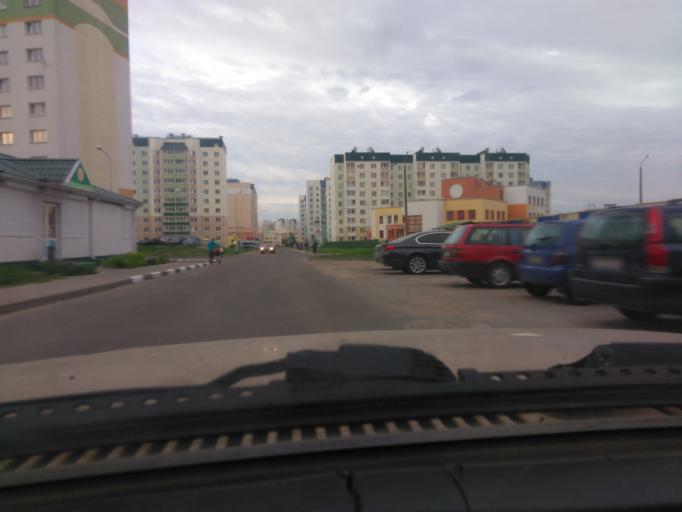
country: BY
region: Mogilev
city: Buynichy
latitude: 53.9136
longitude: 30.2825
